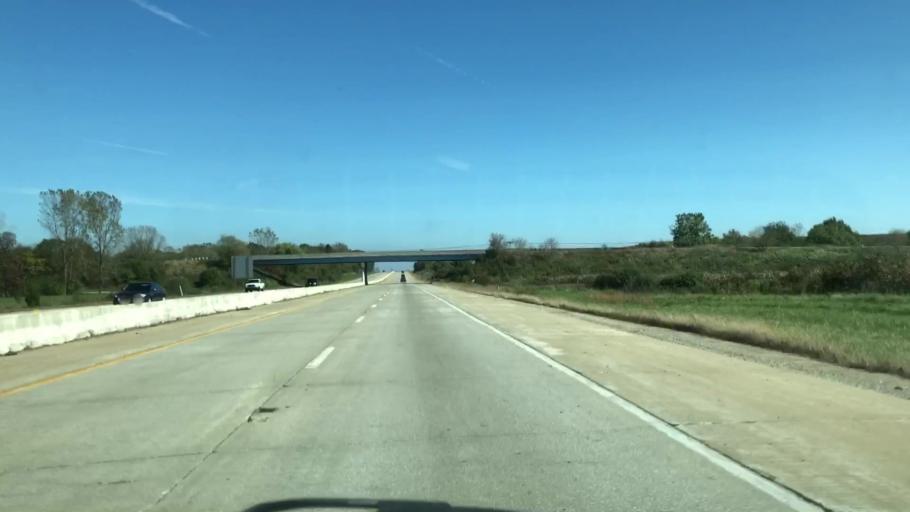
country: US
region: Indiana
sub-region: Elkhart County
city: Elkhart
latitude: 41.6351
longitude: -85.9866
